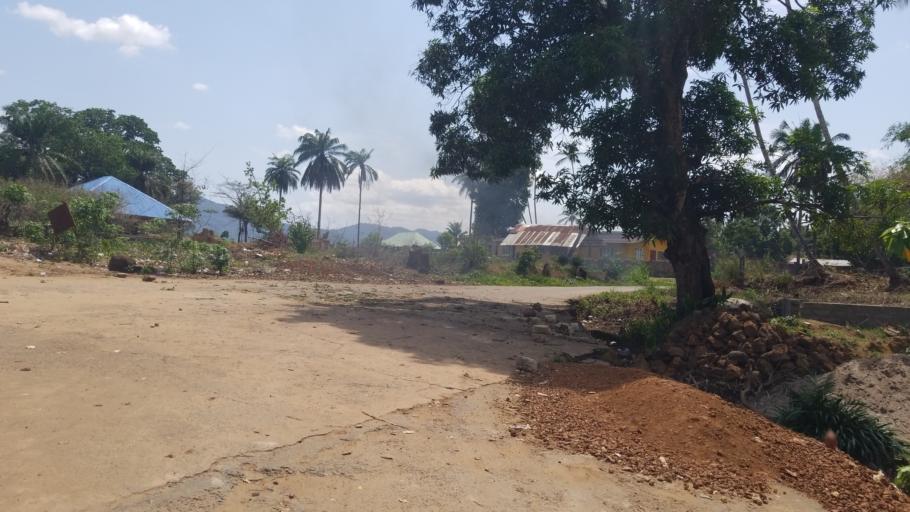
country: SL
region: Western Area
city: Waterloo
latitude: 8.3071
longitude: -13.0507
